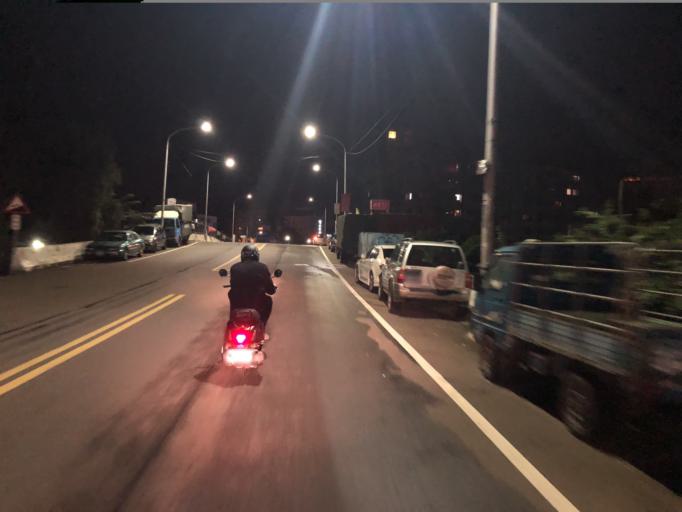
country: TW
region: Taiwan
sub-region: Hsinchu
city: Hsinchu
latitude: 24.7976
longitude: 120.9561
